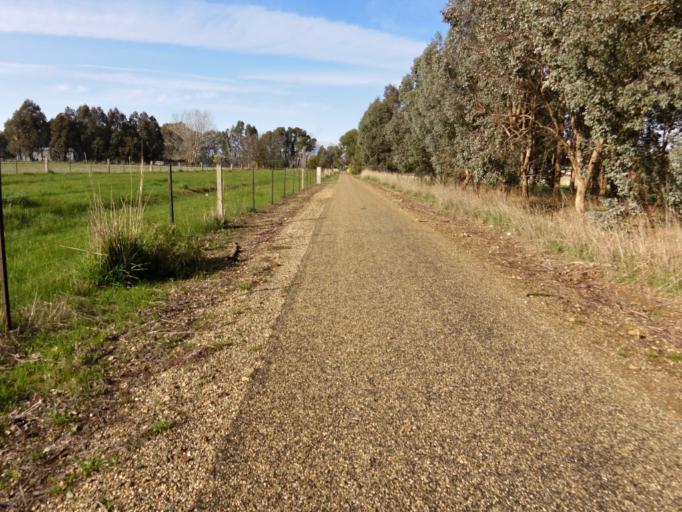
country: AU
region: Victoria
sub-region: Wangaratta
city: Wangaratta
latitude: -36.4278
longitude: 146.5505
